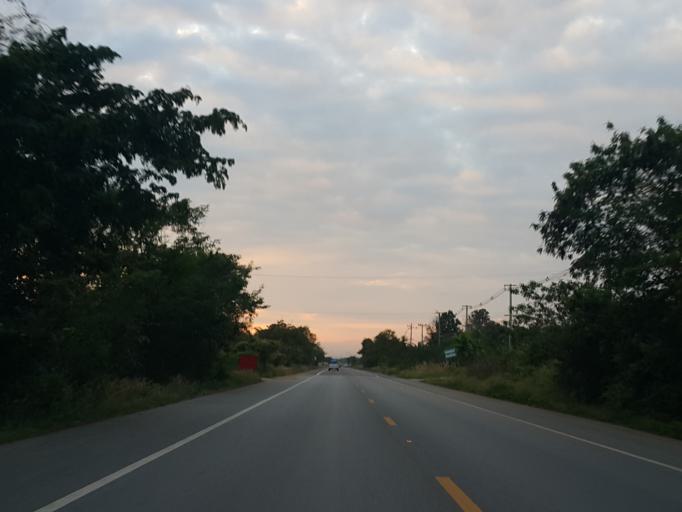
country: TH
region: Lampang
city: Lampang
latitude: 18.2512
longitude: 99.5191
